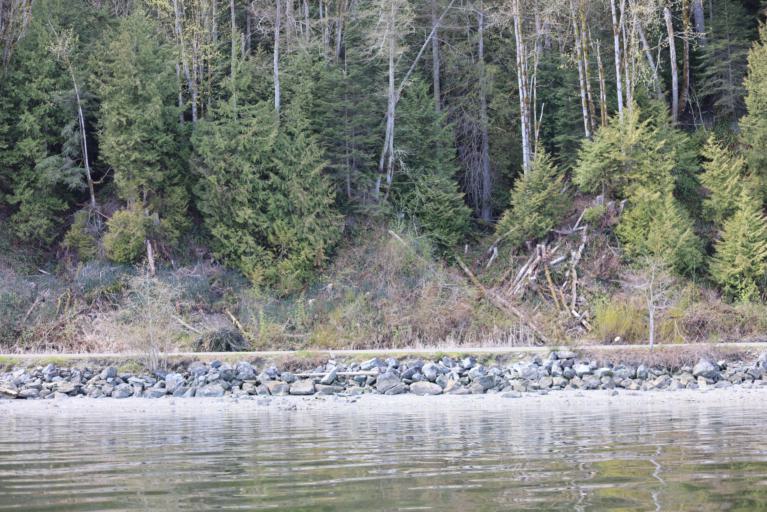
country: CA
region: British Columbia
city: North Saanich
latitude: 48.6207
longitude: -123.5229
